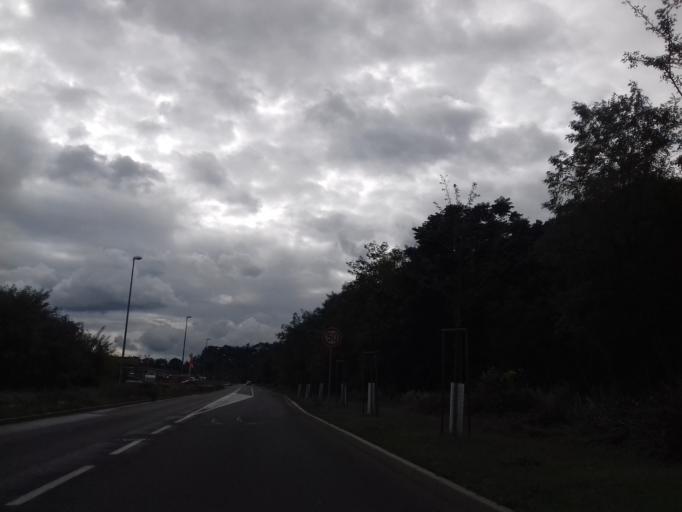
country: CZ
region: Praha
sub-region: Praha 12
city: Modrany
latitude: 50.0199
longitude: 14.3912
